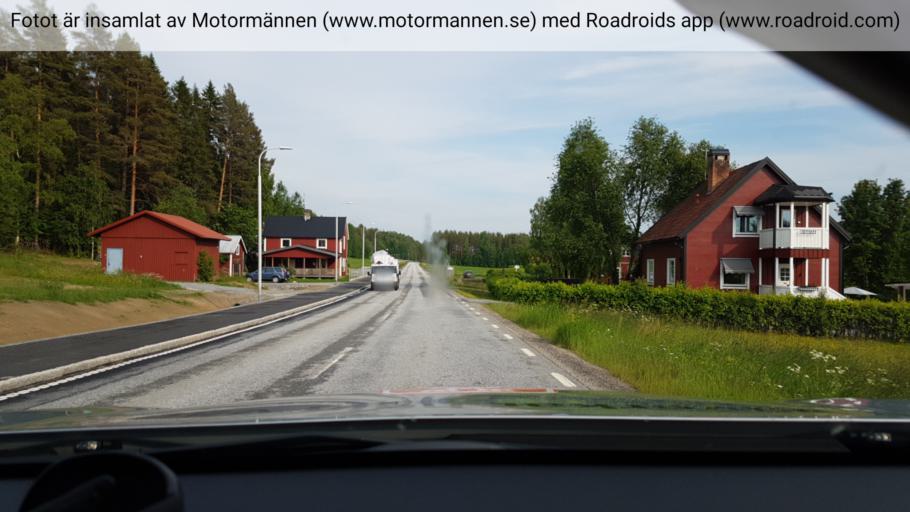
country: SE
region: Vaesterbotten
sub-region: Bjurholms Kommun
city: Bjurholm
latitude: 64.2419
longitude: 19.3297
